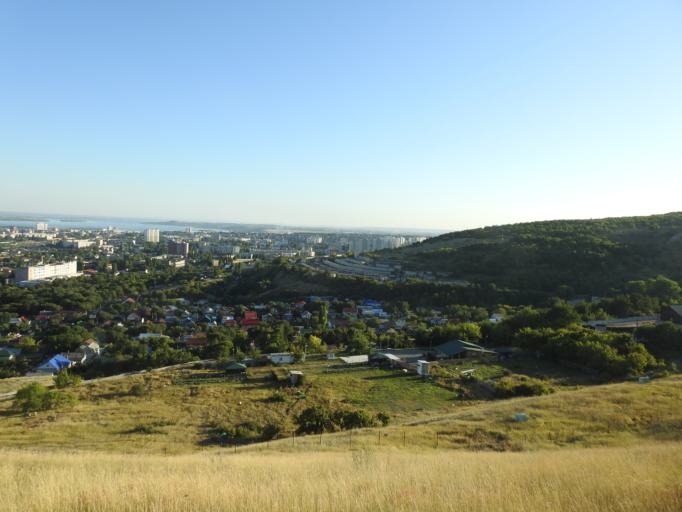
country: RU
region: Saratov
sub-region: Saratovskiy Rayon
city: Saratov
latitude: 51.5503
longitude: 45.9890
